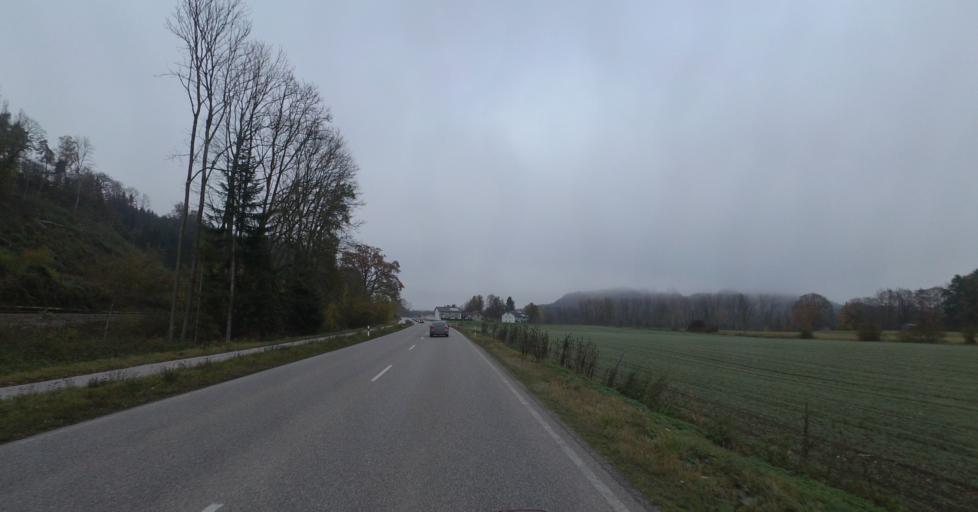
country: DE
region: Bavaria
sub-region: Upper Bavaria
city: Engelsberg
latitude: 48.1103
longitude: 12.5683
